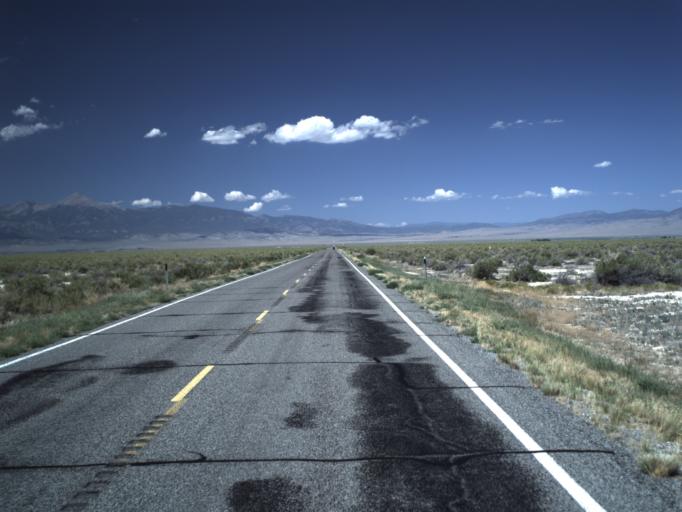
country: US
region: Nevada
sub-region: White Pine County
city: McGill
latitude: 39.0452
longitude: -113.8936
